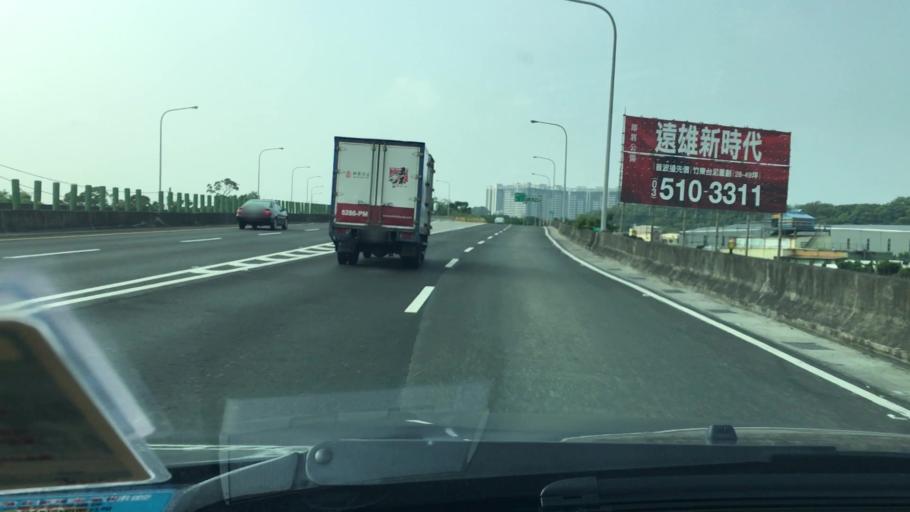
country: TW
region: Taiwan
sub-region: Hsinchu
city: Zhubei
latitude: 24.7797
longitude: 121.0576
